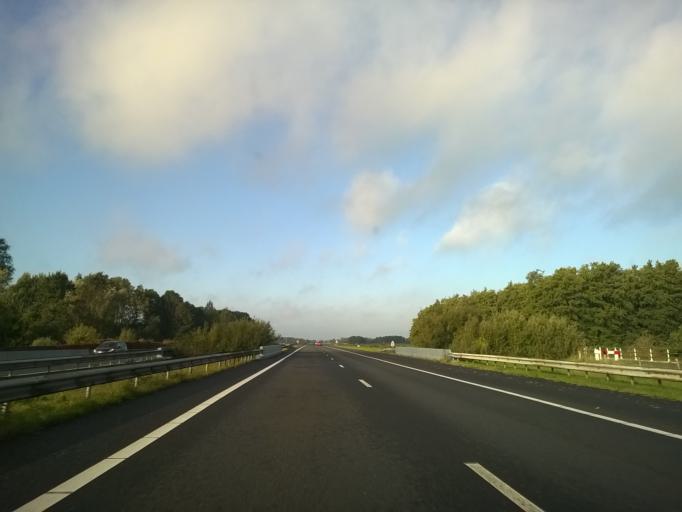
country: NL
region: Groningen
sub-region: Gemeente Leek
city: Leek
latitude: 53.1945
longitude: 6.4161
